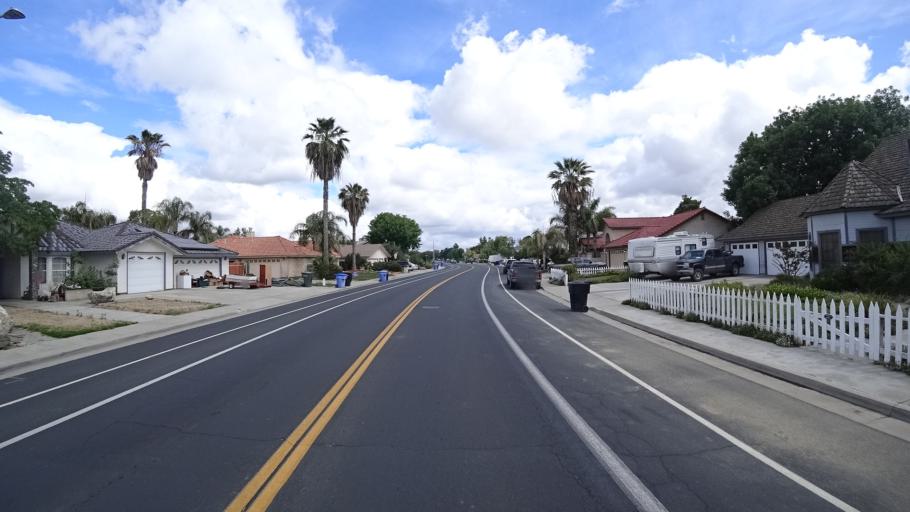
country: US
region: California
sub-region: Kings County
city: Hanford
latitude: 36.3368
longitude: -119.6658
